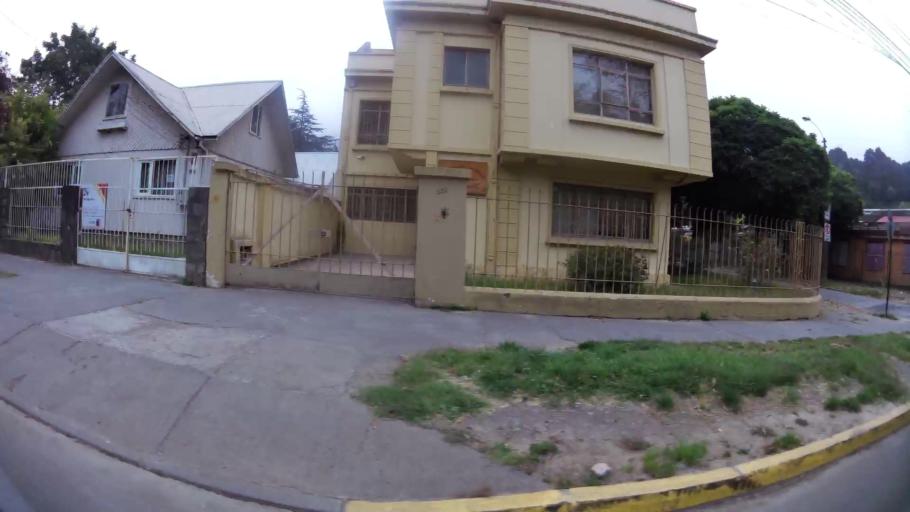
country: CL
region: Biobio
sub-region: Provincia de Concepcion
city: Concepcion
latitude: -36.8326
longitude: -73.0357
